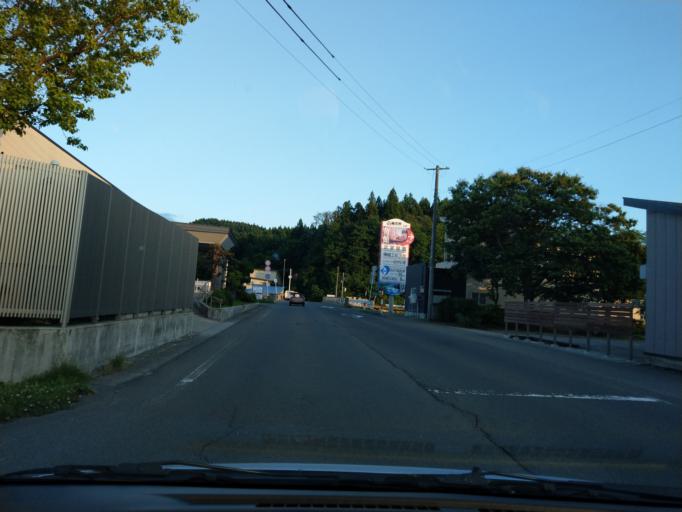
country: JP
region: Akita
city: Kakunodatemachi
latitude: 39.6105
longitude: 140.5701
